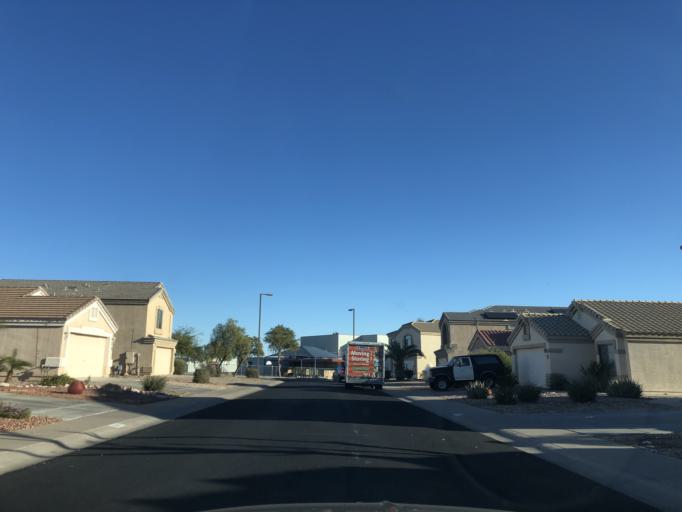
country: US
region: Arizona
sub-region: Maricopa County
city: Buckeye
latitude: 33.4397
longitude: -112.5647
